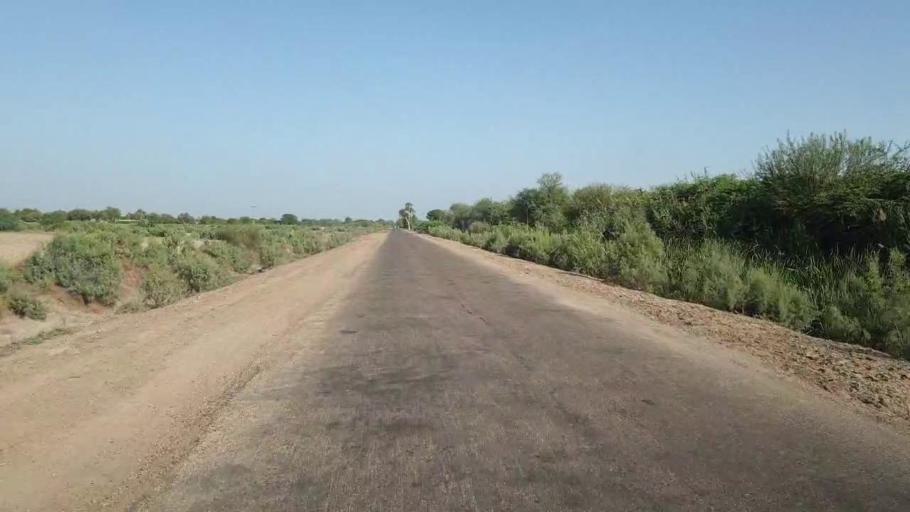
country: PK
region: Sindh
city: Nawabshah
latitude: 26.3858
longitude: 68.4540
